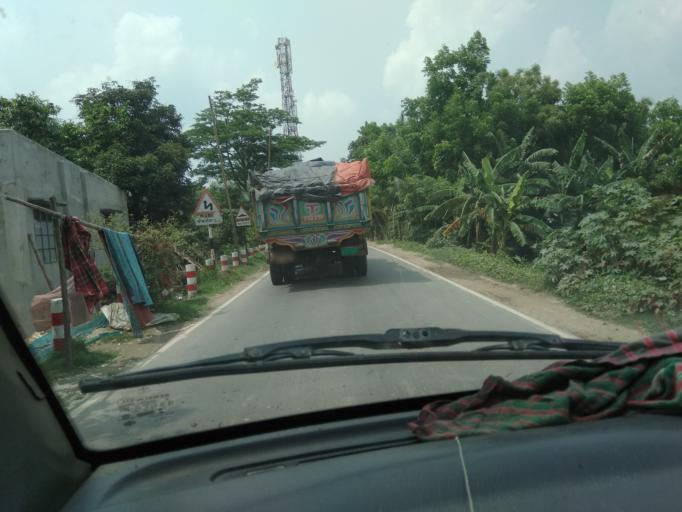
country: BD
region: Dhaka
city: Char Bhadrasan
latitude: 23.4101
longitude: 90.2157
